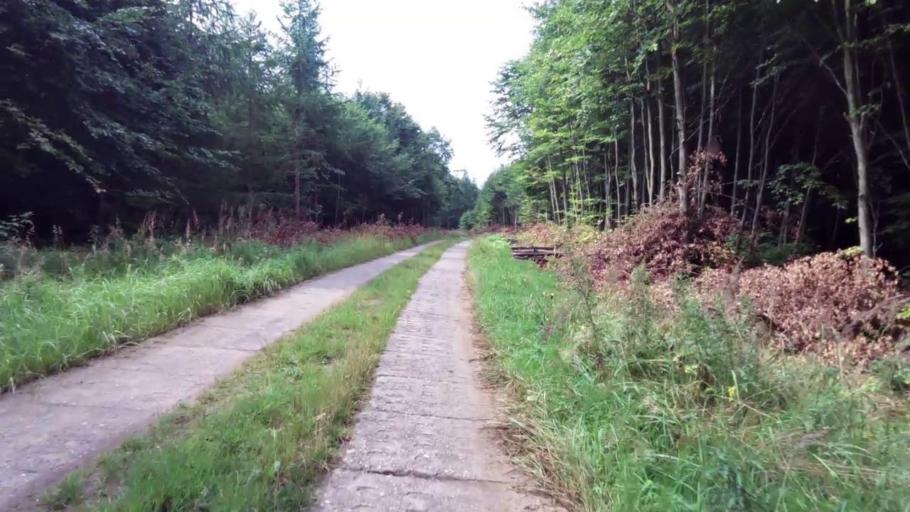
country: PL
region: West Pomeranian Voivodeship
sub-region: Powiat szczecinecki
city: Lubowo
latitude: 53.6013
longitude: 16.3098
